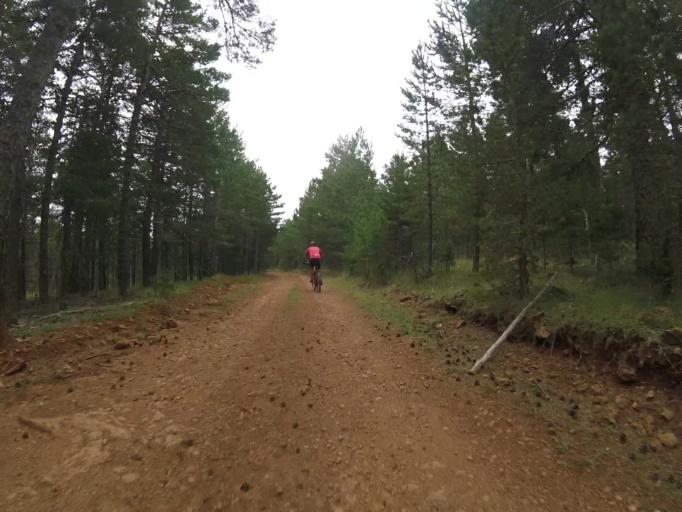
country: ES
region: Aragon
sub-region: Provincia de Teruel
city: Valdelinares
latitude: 40.3613
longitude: -0.6147
